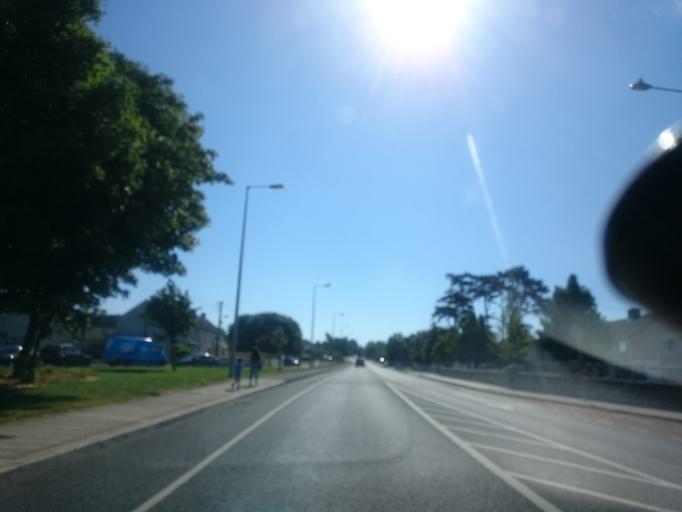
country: IE
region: Leinster
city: Monkstown
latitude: 53.2865
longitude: -6.1660
